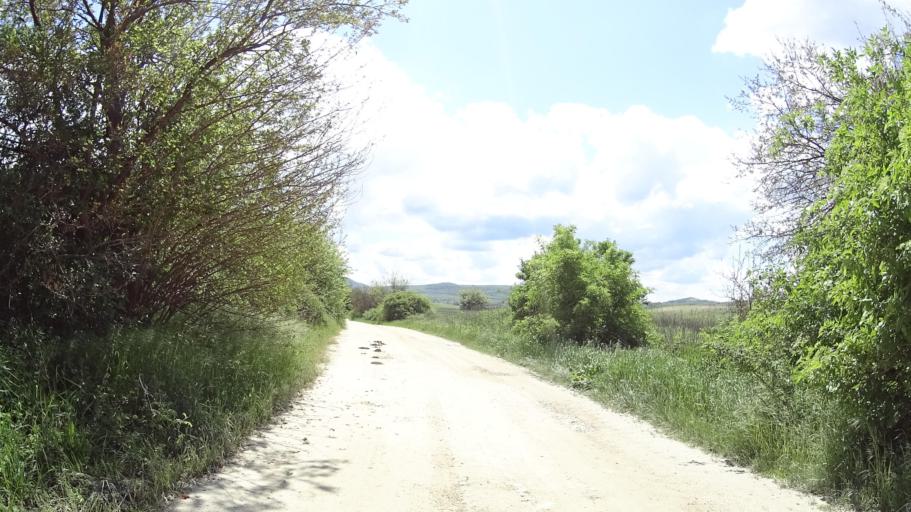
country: HU
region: Komarom-Esztergom
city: Kesztolc
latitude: 47.6962
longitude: 18.7972
